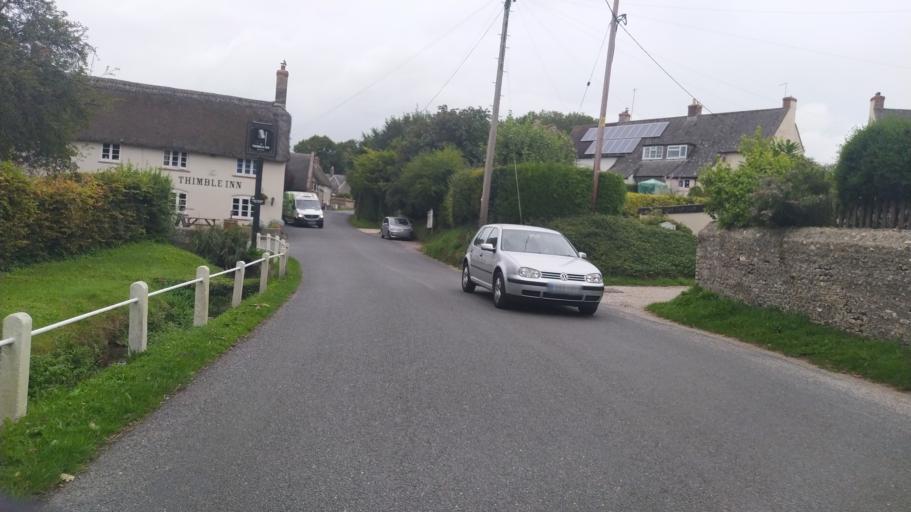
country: GB
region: England
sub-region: Dorset
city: Dorchester
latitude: 50.7765
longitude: -2.4068
